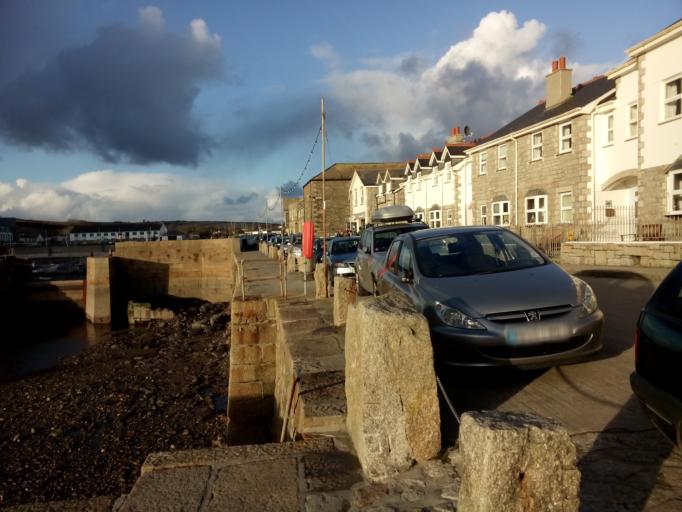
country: GB
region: England
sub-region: Cornwall
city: Porthleven
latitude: 50.0833
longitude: -5.3157
